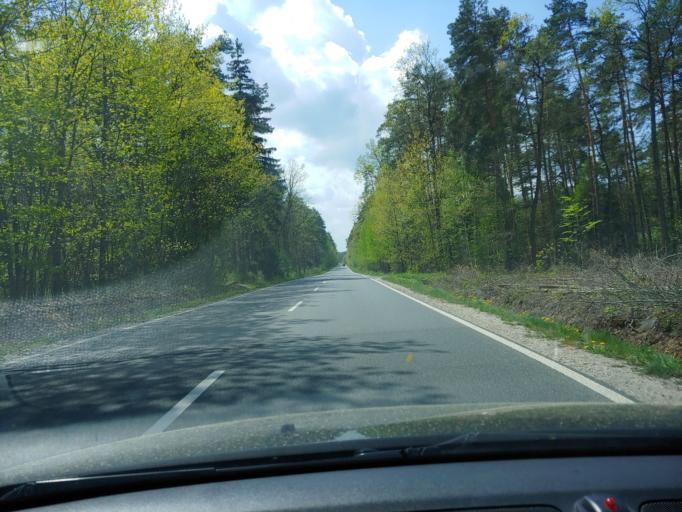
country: PL
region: Lesser Poland Voivodeship
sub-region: Powiat tarnowski
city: Jodlowka-Walki
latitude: 50.1189
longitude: 21.1263
